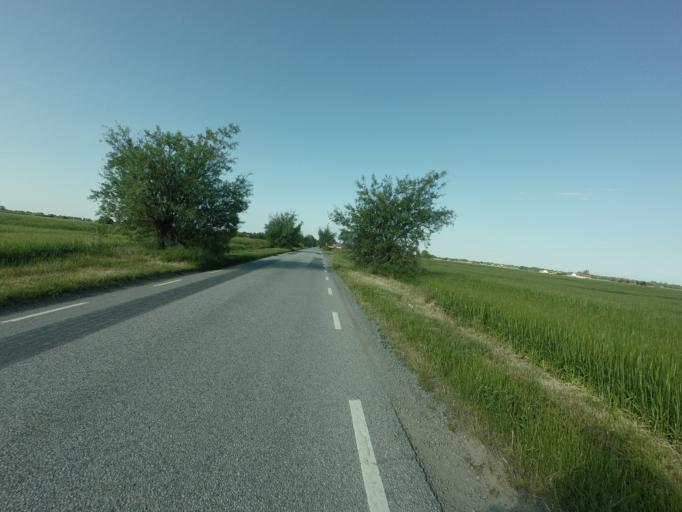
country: SE
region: Skane
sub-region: Trelleborgs Kommun
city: Skare
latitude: 55.4174
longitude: 13.0153
